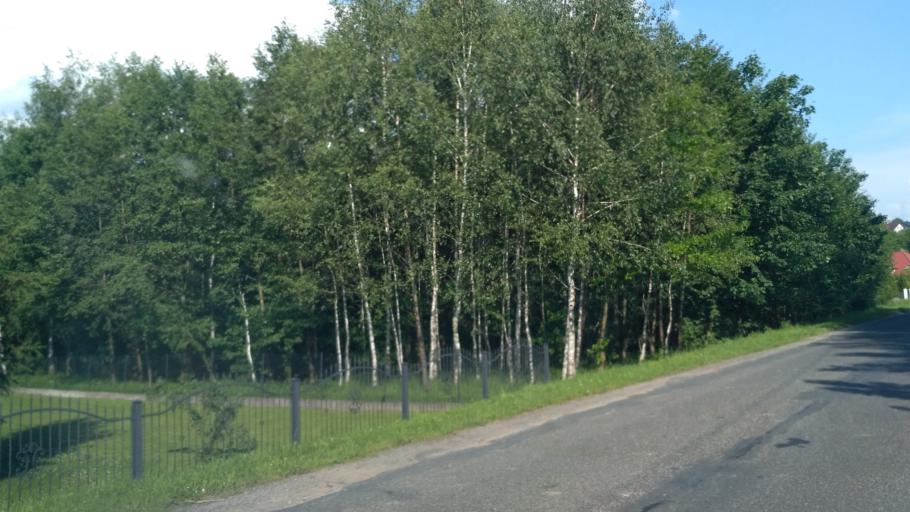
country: PL
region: Subcarpathian Voivodeship
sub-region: Powiat jaroslawski
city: Kramarzowka
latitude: 49.8746
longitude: 22.5080
